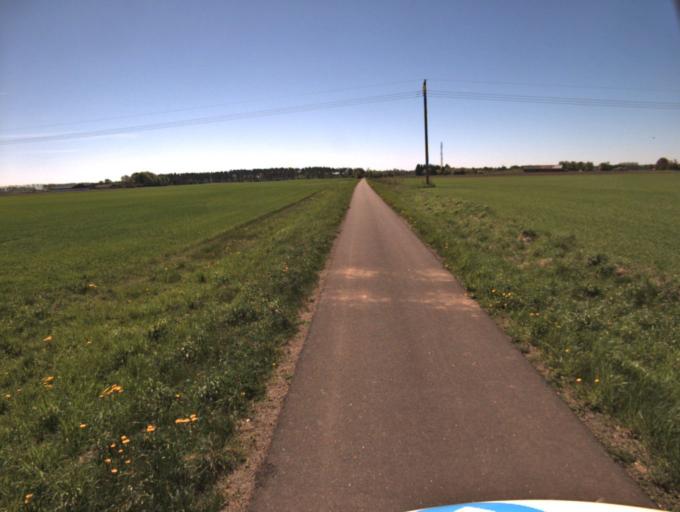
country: SE
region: Skane
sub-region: Kristianstads Kommun
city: Norra Asum
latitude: 55.9610
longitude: 14.1577
